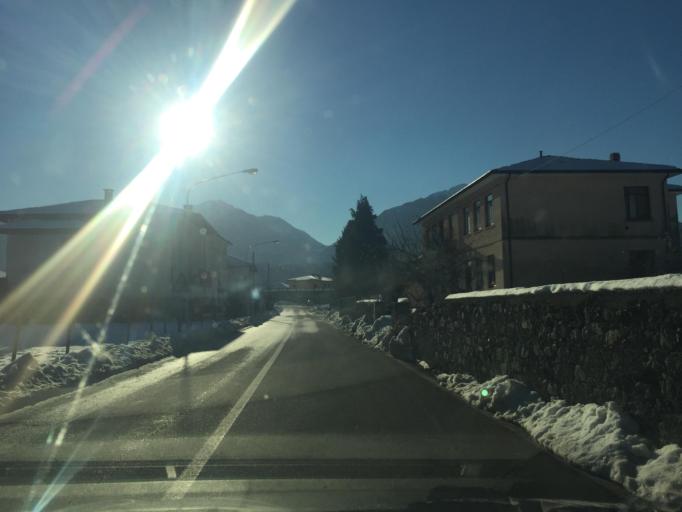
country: IT
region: Friuli Venezia Giulia
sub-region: Provincia di Udine
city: Tolmezzo
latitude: 46.4119
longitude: 13.0053
